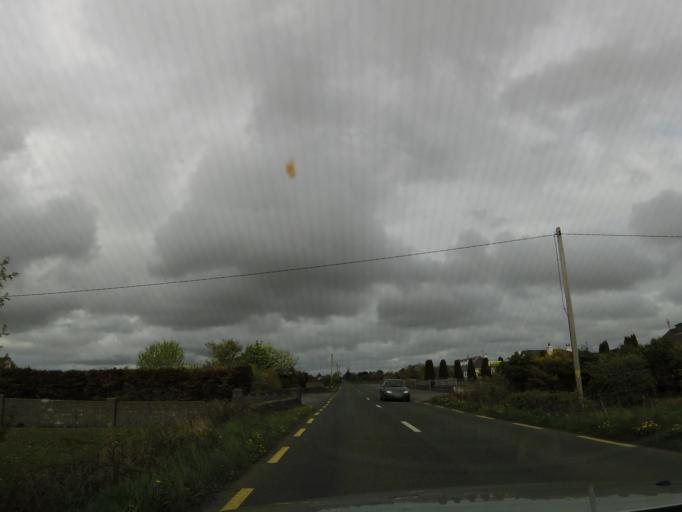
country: IE
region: Connaught
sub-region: Maigh Eo
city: Ballinrobe
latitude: 53.6344
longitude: -9.1918
